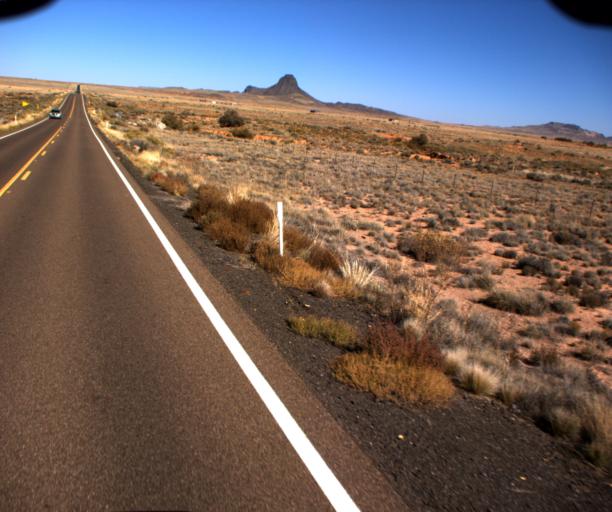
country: US
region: Arizona
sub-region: Navajo County
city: Dilkon
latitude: 35.2556
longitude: -110.4298
